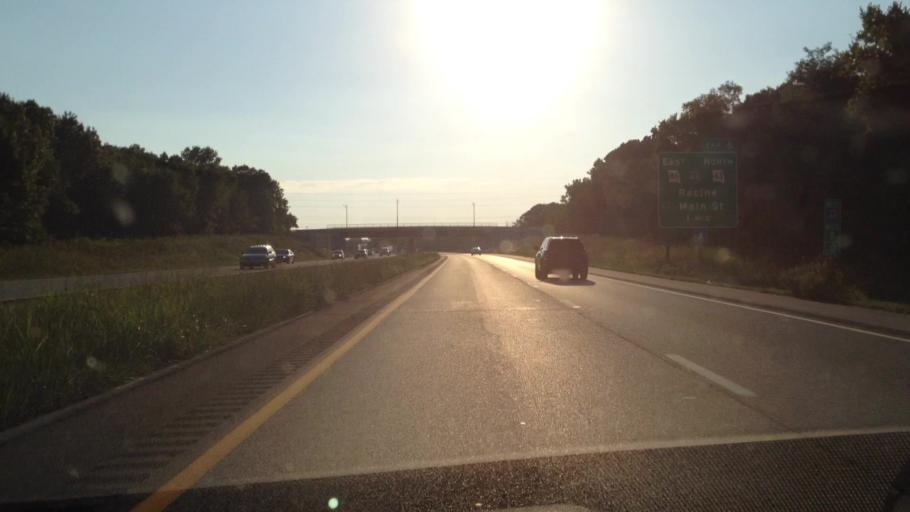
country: US
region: Missouri
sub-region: Jasper County
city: Joplin
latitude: 37.0459
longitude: -94.4931
